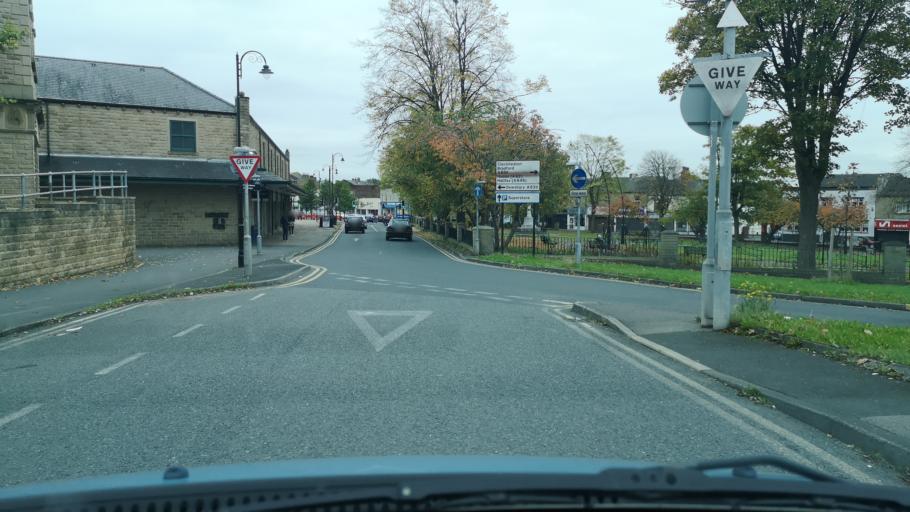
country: GB
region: England
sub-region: Kirklees
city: Heckmondwike
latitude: 53.7087
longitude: -1.6769
